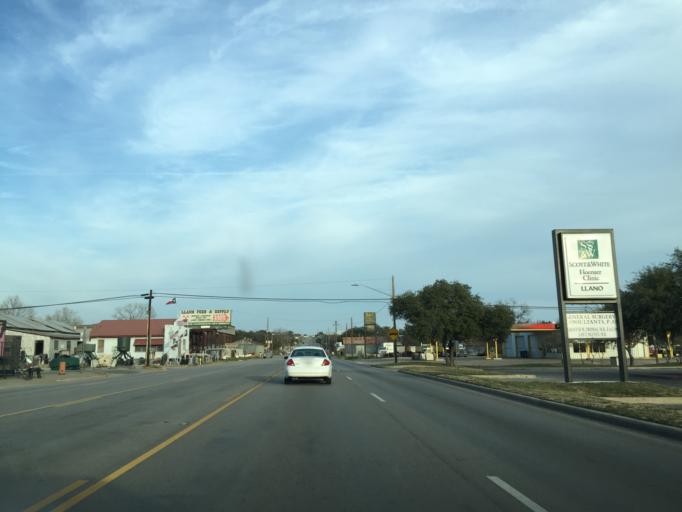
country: US
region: Texas
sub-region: Llano County
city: Llano
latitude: 30.7595
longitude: -98.6745
